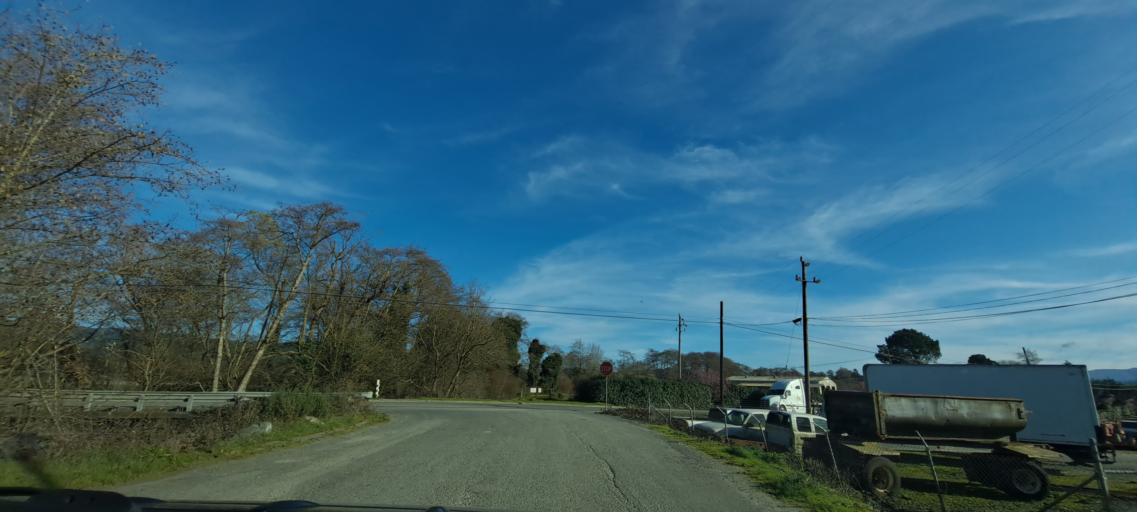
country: US
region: California
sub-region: Humboldt County
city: Fortuna
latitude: 40.5855
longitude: -124.1550
